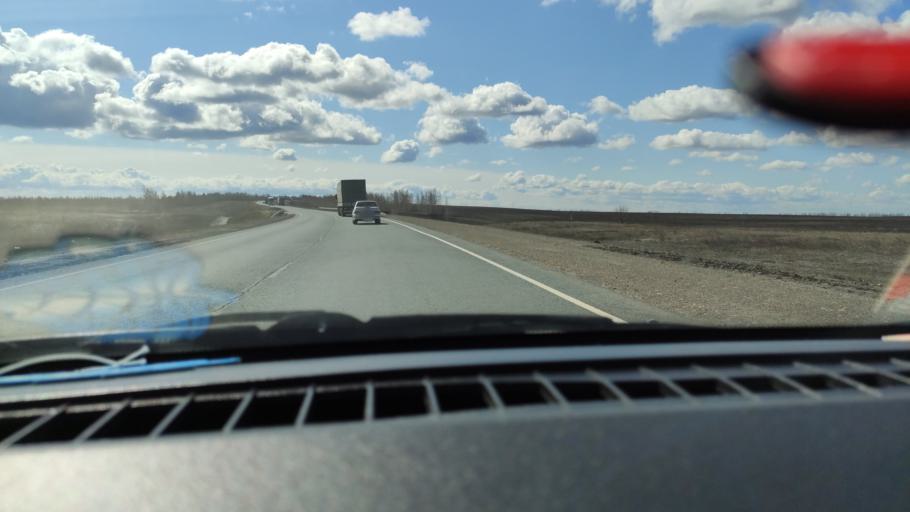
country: RU
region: Samara
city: Syzran'
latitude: 52.9393
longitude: 48.3062
